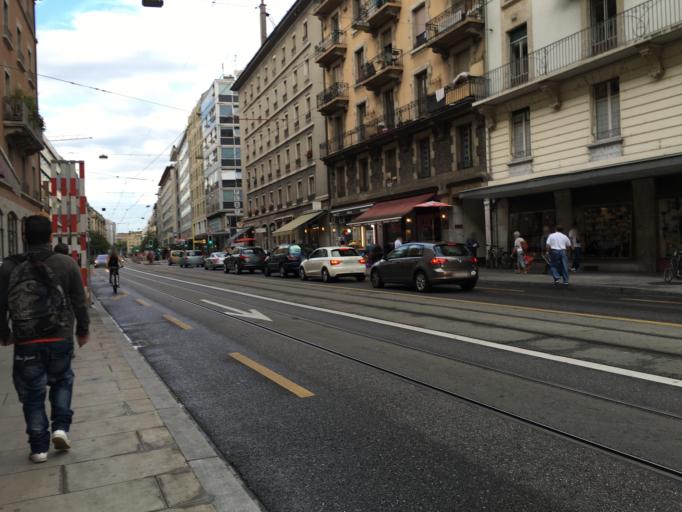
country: CH
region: Geneva
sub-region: Geneva
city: Geneve
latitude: 46.2123
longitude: 6.1450
